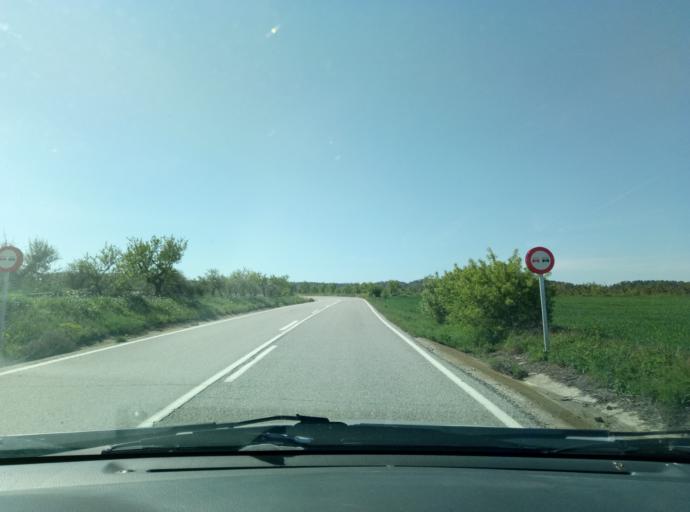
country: ES
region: Catalonia
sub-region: Provincia de Lleida
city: Vallbona de les Monges
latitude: 41.5475
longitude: 1.0265
